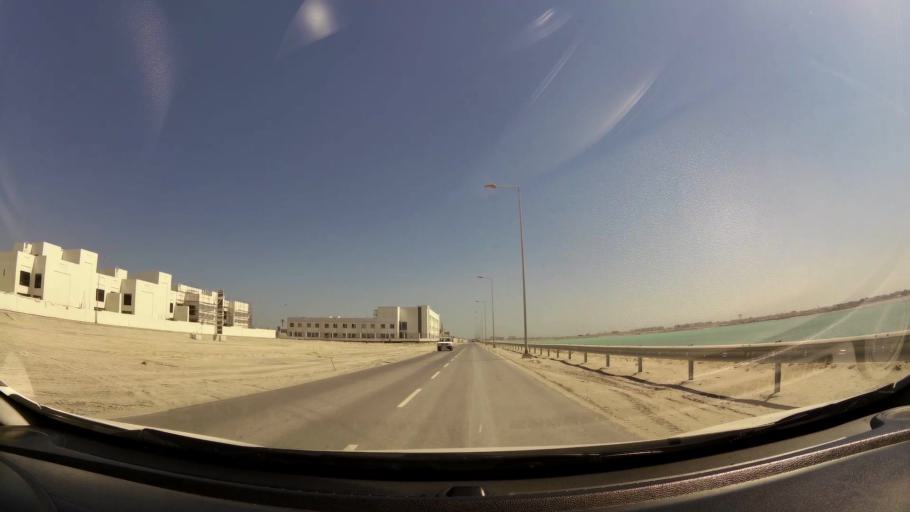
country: BH
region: Muharraq
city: Al Muharraq
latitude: 26.2994
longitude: 50.6340
